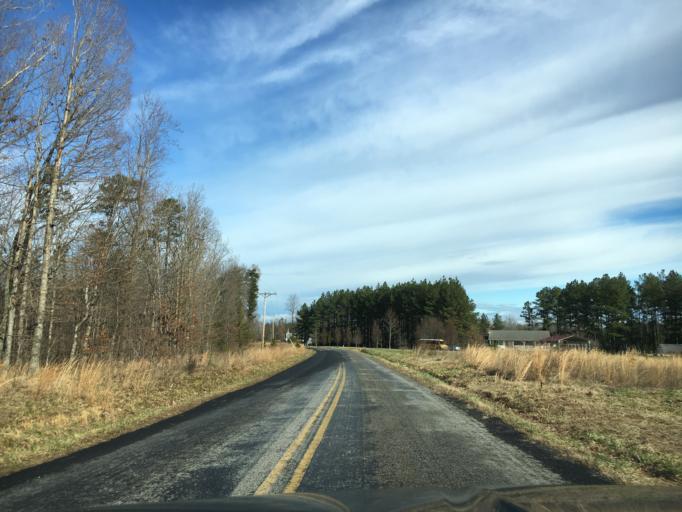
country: US
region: Virginia
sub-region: Nottoway County
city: Crewe
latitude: 37.3034
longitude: -78.1960
